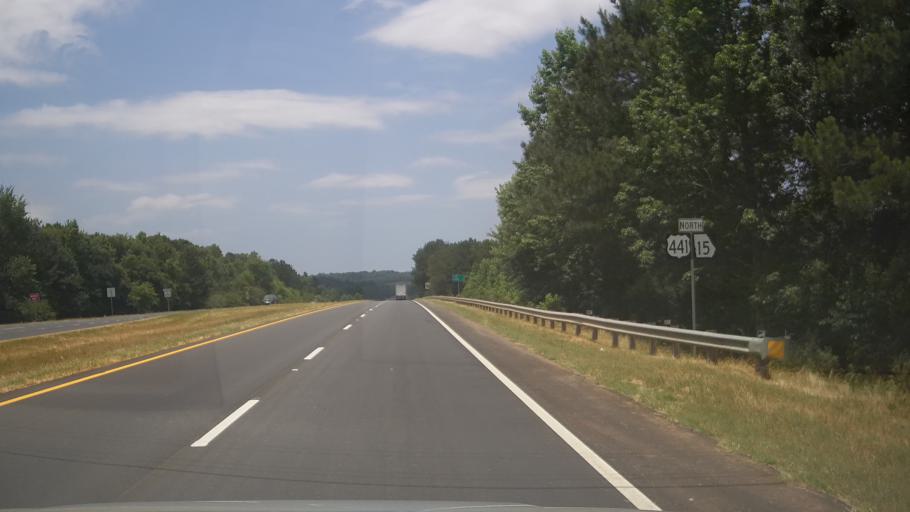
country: US
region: Georgia
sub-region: Jackson County
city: Commerce
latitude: 34.2135
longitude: -83.4419
